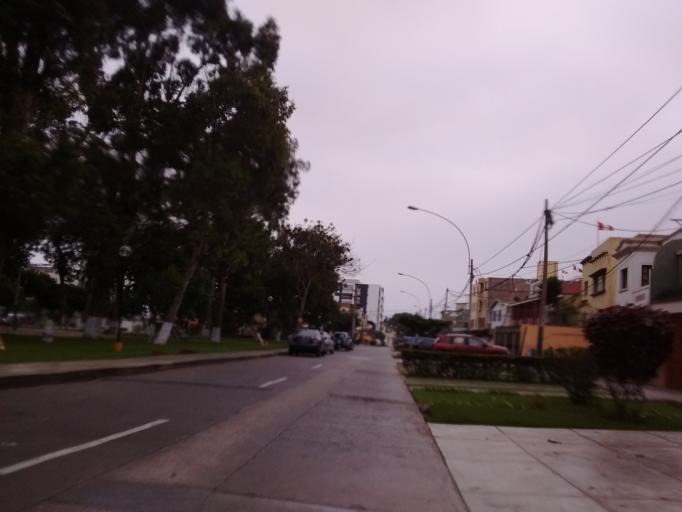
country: PE
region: Lima
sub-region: Lima
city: San Isidro
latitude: -12.0736
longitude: -77.0692
